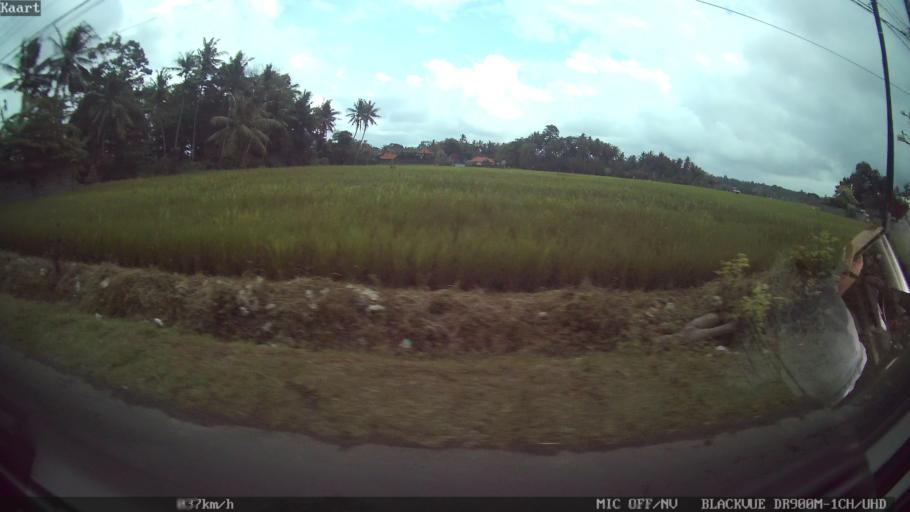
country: ID
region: Bali
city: Banjar Mambalkajanan
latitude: -8.5493
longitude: 115.2122
